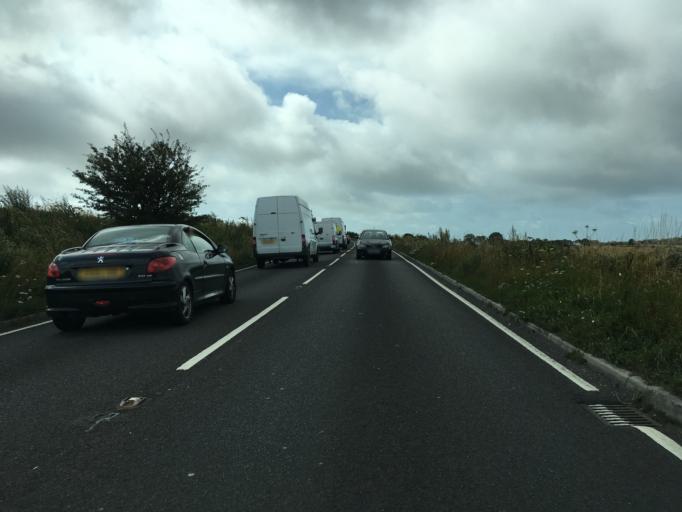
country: GB
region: England
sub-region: Brighton and Hove
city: Rottingdean
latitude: 50.8425
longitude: -0.0741
